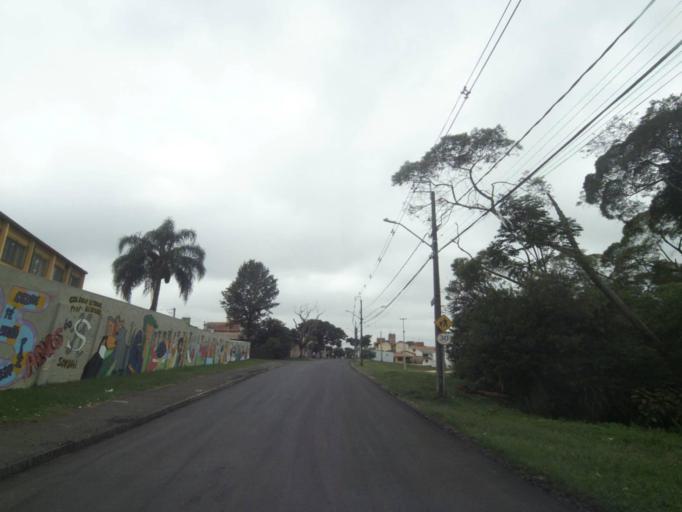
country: BR
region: Parana
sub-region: Curitiba
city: Curitiba
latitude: -25.4876
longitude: -49.3534
